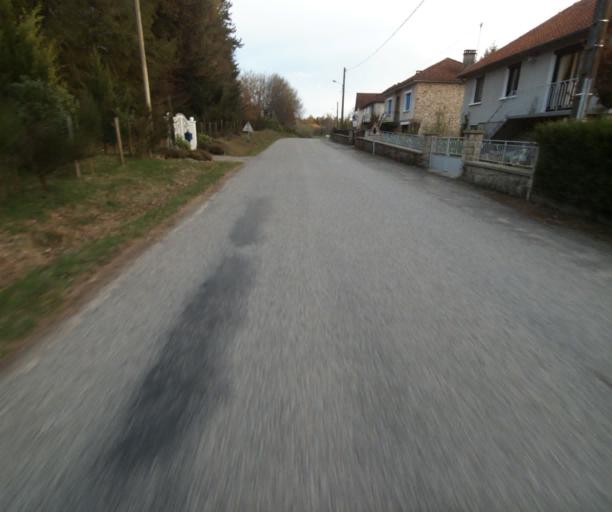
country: FR
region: Limousin
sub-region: Departement de la Correze
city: Correze
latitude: 45.2708
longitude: 1.9771
